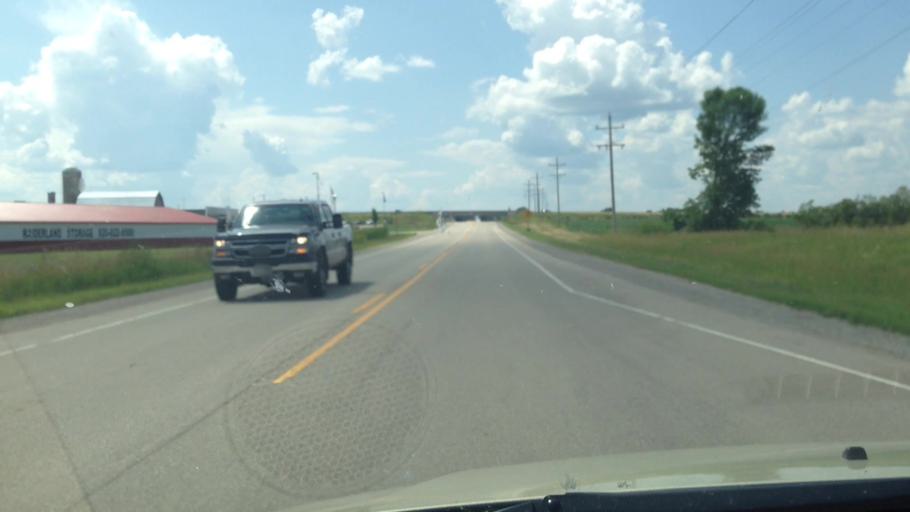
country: US
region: Wisconsin
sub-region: Brown County
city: Pulaski
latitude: 44.6737
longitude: -88.3018
